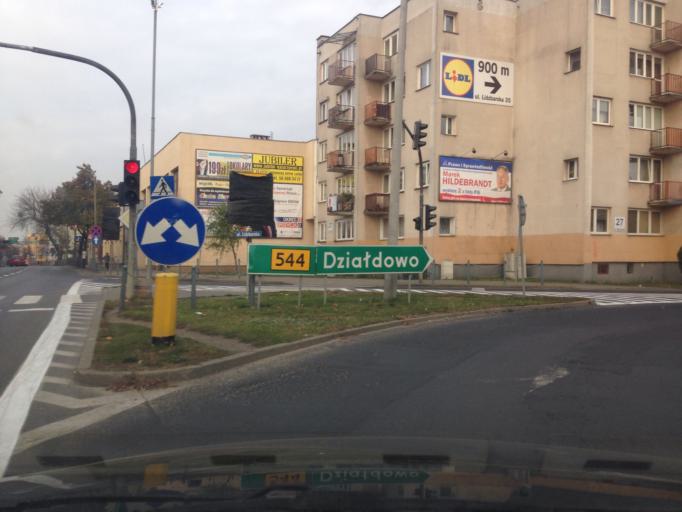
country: PL
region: Kujawsko-Pomorskie
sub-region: Powiat brodnicki
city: Brodnica
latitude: 53.2504
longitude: 19.3999
